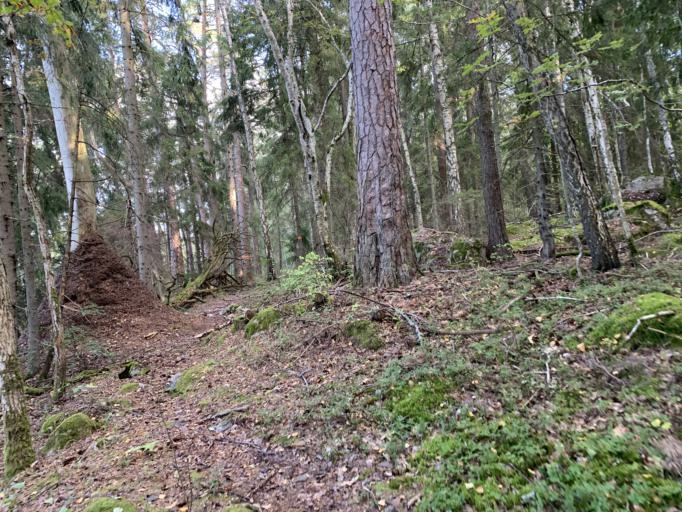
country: SE
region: Vaestmanland
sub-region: Hallstahammars Kommun
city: Kolback
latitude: 59.4819
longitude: 16.2321
